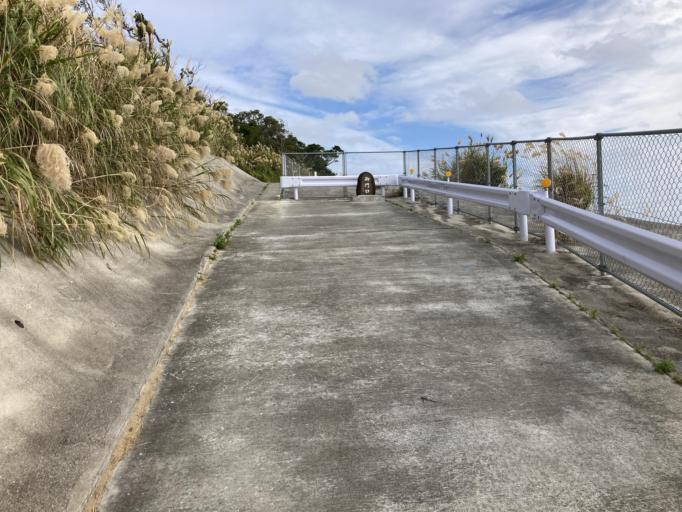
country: JP
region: Okinawa
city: Ginowan
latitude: 26.2060
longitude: 127.7495
